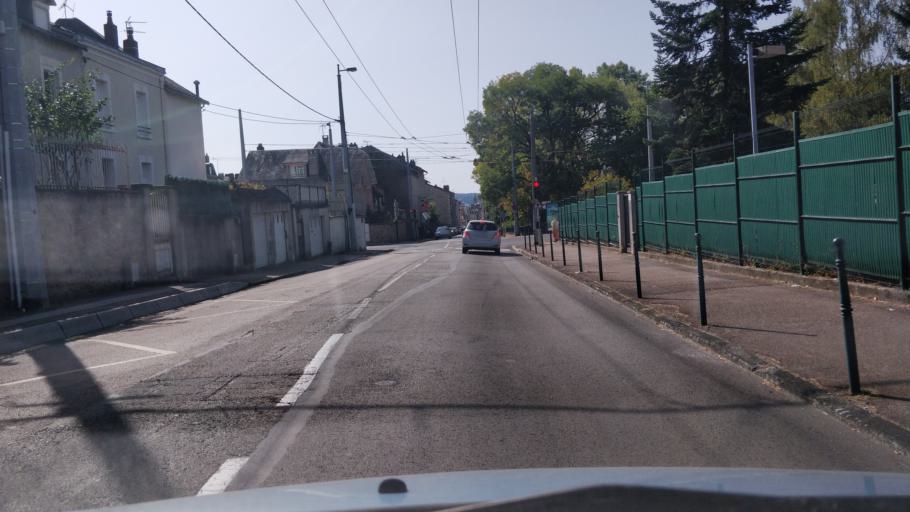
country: FR
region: Limousin
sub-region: Departement de la Haute-Vienne
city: Limoges
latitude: 45.8461
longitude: 1.2557
